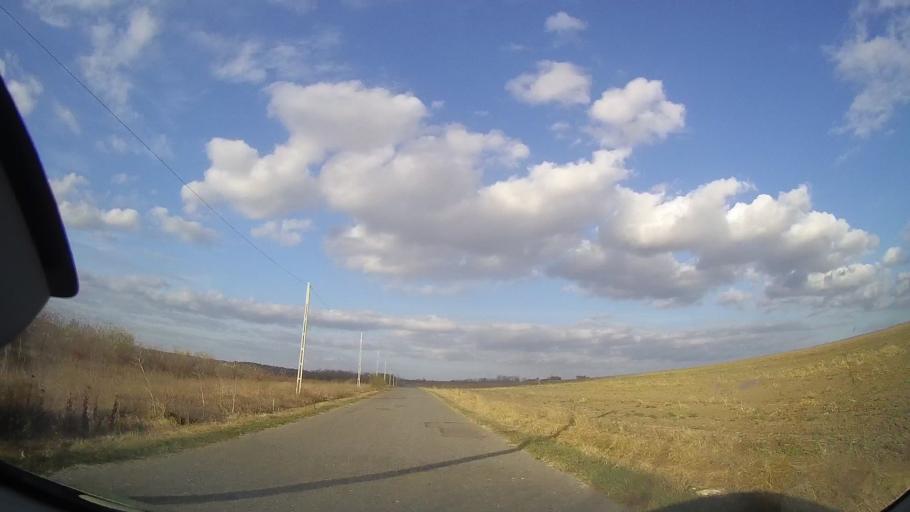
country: RO
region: Constanta
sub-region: Comuna Cerchezu
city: Cerchezu
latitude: 43.8478
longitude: 28.0992
